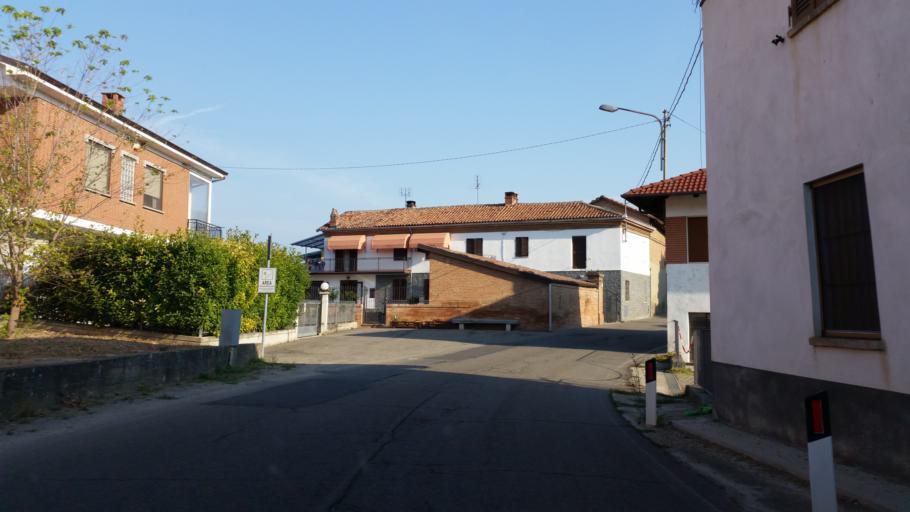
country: IT
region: Piedmont
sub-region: Provincia di Asti
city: Coazzolo
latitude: 44.7261
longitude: 8.1461
